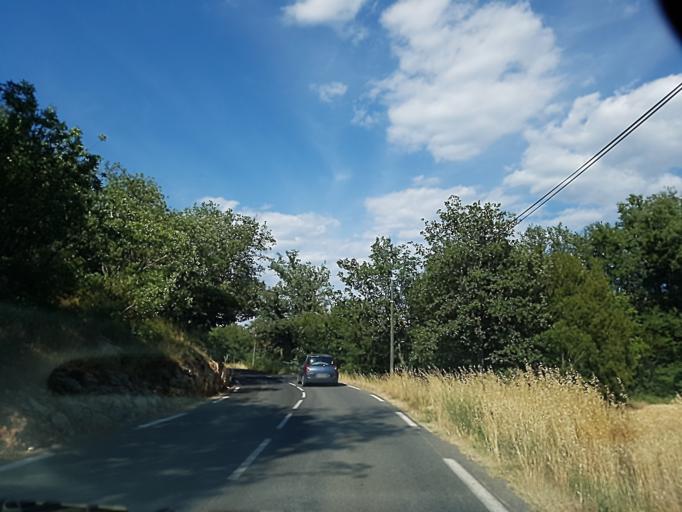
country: FR
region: Provence-Alpes-Cote d'Azur
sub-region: Departement du Var
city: Bras
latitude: 43.4602
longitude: 5.9315
